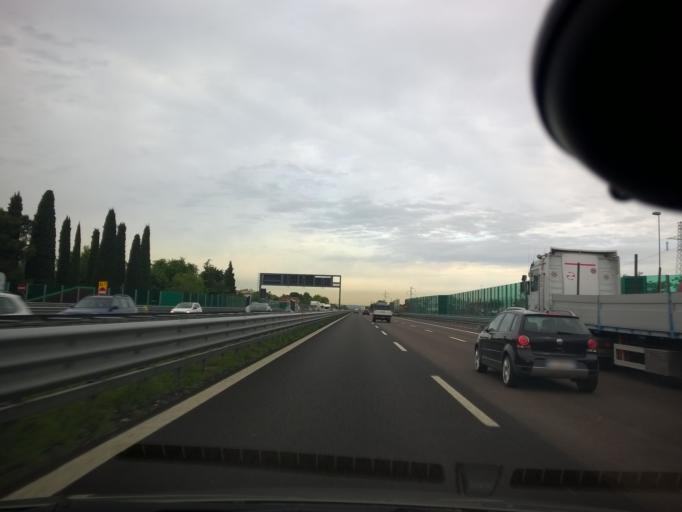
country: IT
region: Veneto
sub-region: Provincia di Verona
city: Peschiera del Garda
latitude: 45.4302
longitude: 10.6743
